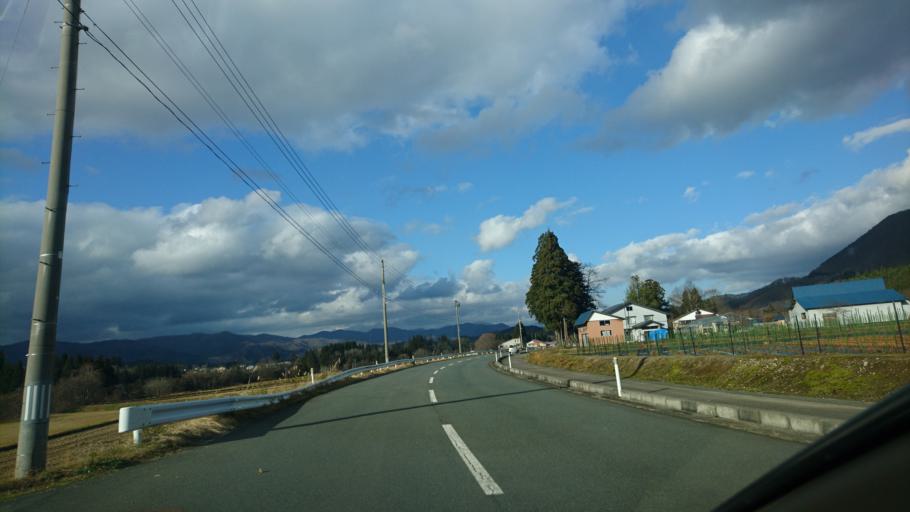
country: JP
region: Akita
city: Yokotemachi
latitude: 39.3854
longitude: 140.7649
